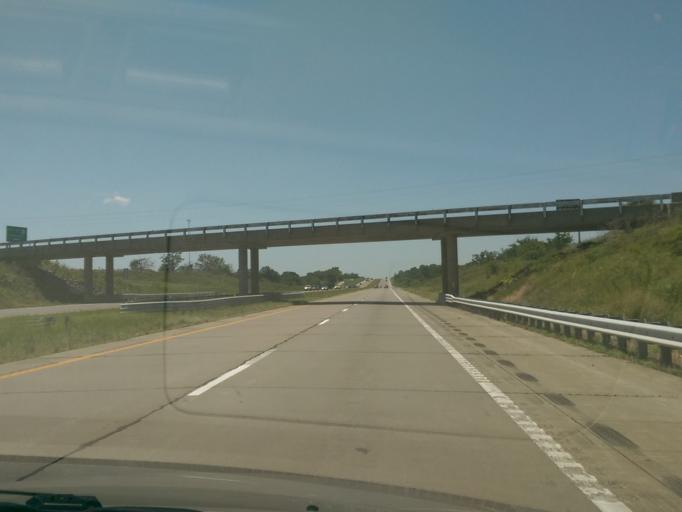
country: US
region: Missouri
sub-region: Saline County
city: Marshall
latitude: 38.9532
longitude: -93.0878
